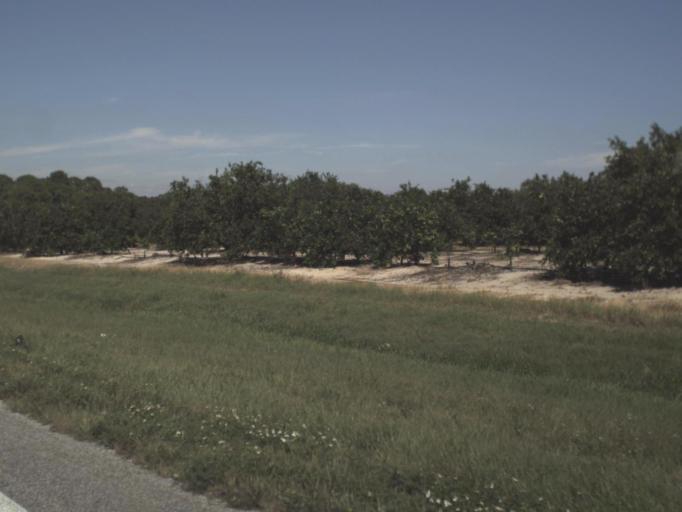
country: US
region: Florida
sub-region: Highlands County
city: Lake Placid
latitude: 27.3421
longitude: -81.3864
